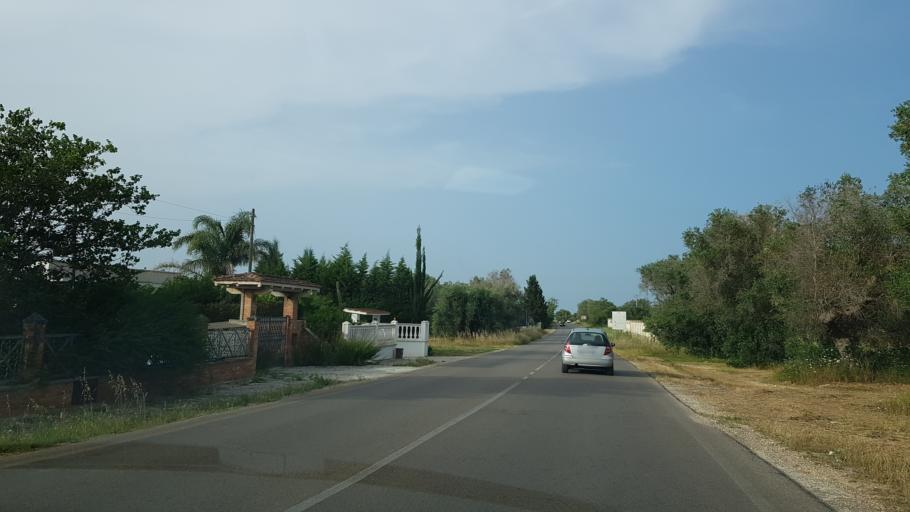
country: IT
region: Apulia
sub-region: Provincia di Brindisi
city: San Pietro Vernotico
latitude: 40.4794
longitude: 17.9814
